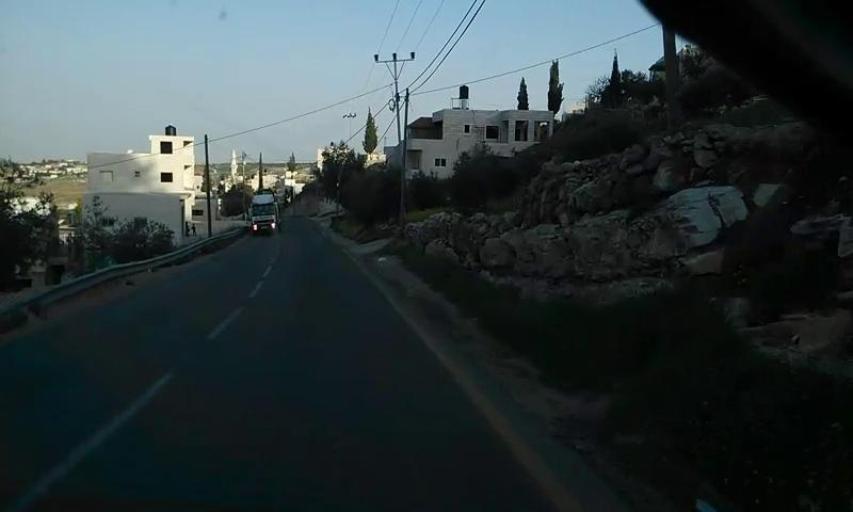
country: PS
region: West Bank
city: Jannatah
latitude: 31.6520
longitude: 35.2088
